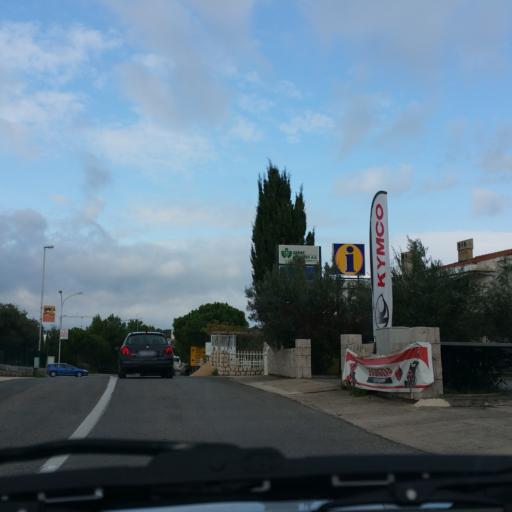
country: HR
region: Primorsko-Goranska
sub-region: Grad Krk
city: Krk
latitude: 45.0317
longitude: 14.5717
